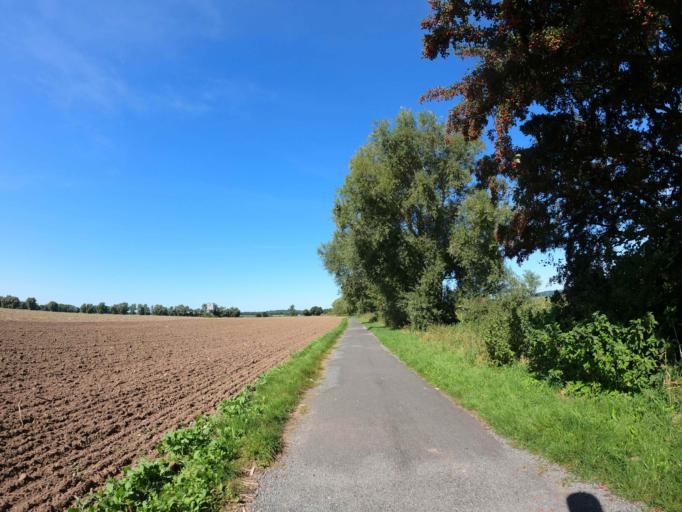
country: DE
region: Mecklenburg-Vorpommern
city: Prohn
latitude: 54.3898
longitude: 13.0354
